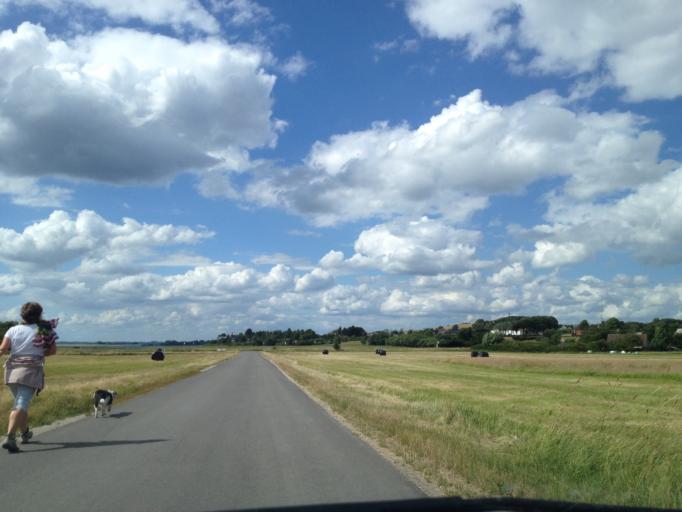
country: DK
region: Central Jutland
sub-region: Syddjurs Kommune
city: Ronde
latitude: 56.2061
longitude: 10.4844
